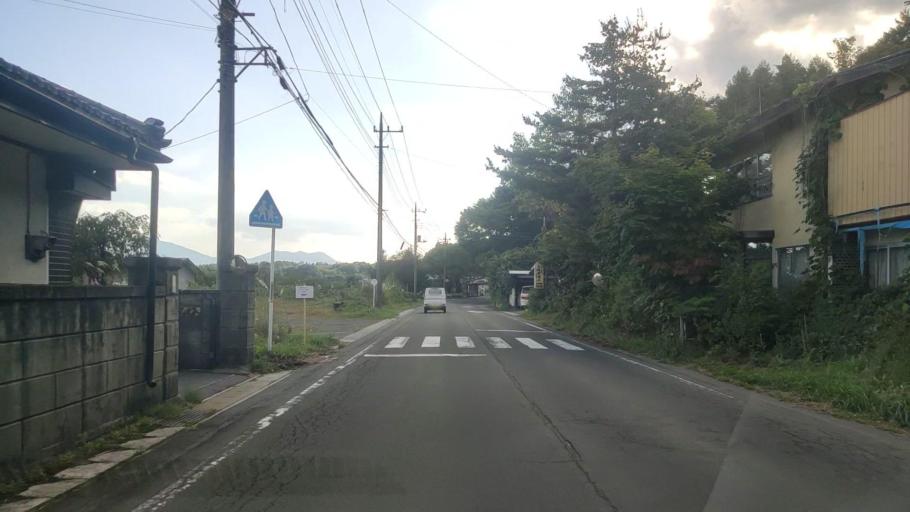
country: JP
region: Nagano
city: Nakano
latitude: 36.5877
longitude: 138.5746
